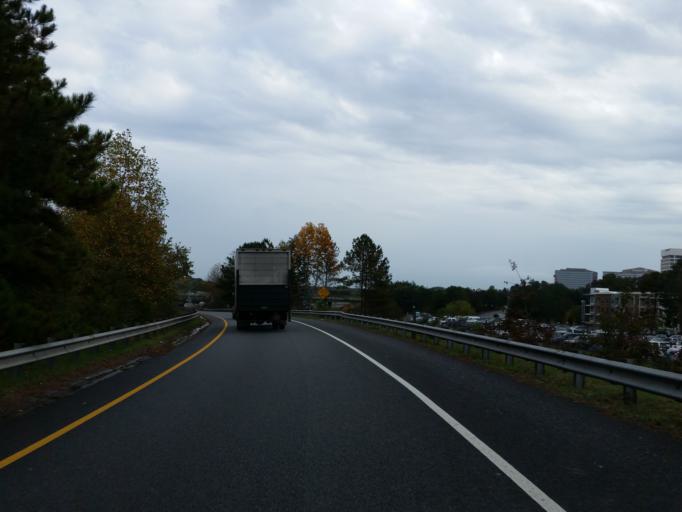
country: US
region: Georgia
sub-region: Cobb County
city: Vinings
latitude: 33.8970
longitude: -84.4695
